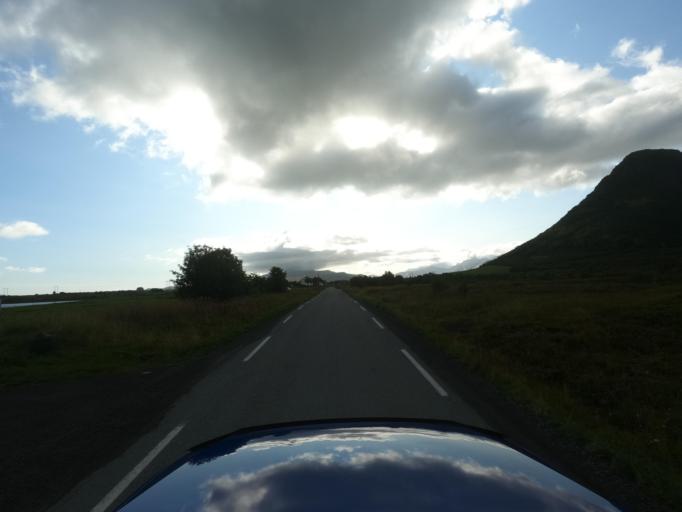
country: NO
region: Nordland
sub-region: Vestvagoy
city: Gravdal
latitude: 68.1660
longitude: 13.5481
